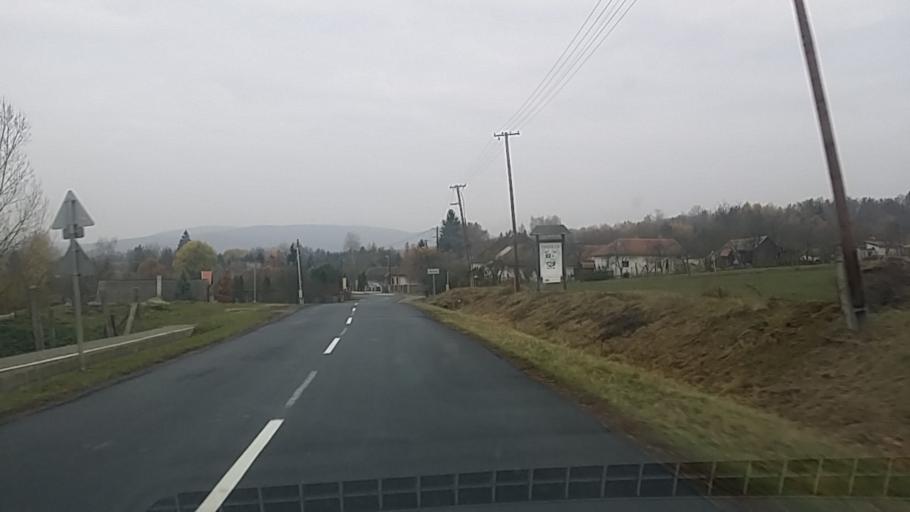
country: HU
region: Borsod-Abauj-Zemplen
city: Sarospatak
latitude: 48.4727
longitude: 21.4745
